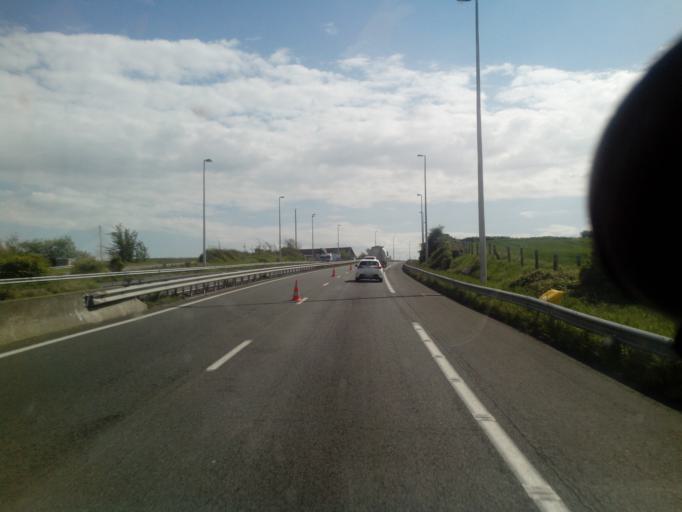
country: FR
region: Nord-Pas-de-Calais
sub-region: Departement du Pas-de-Calais
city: Marquise
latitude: 50.7962
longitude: 1.6883
